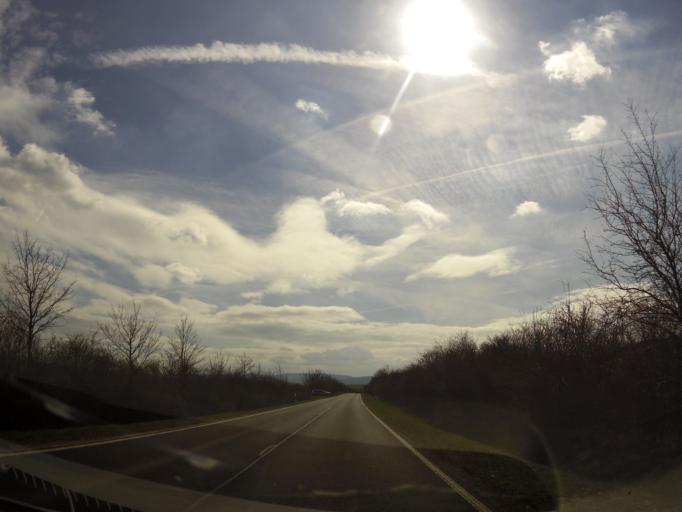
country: DE
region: Thuringia
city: Crawinkel
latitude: 50.7766
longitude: 10.7904
